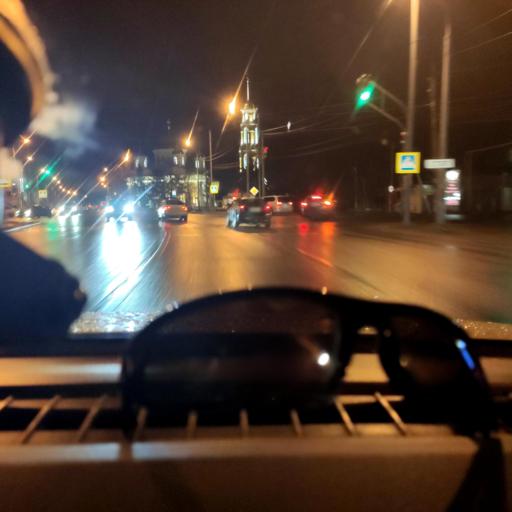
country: RU
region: Samara
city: Volzhskiy
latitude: 53.4267
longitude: 50.1209
